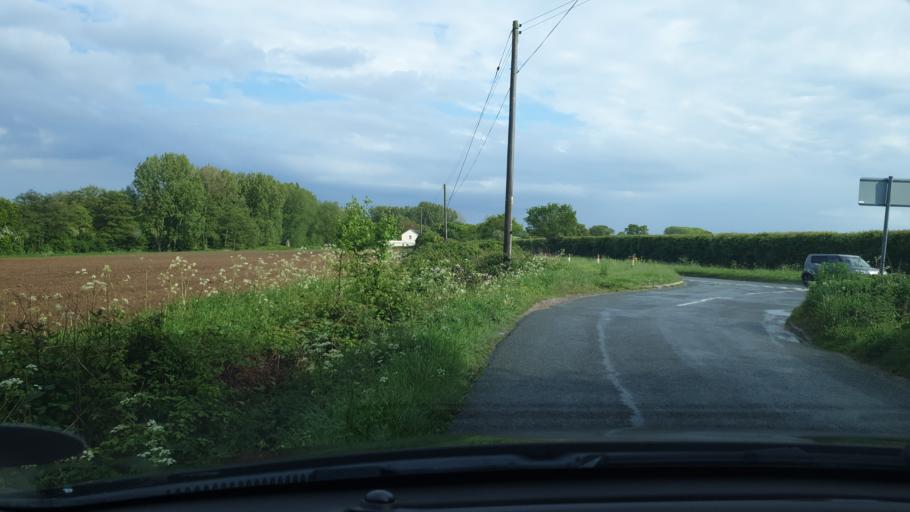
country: GB
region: England
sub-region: Essex
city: Great Bentley
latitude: 51.8356
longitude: 1.0544
